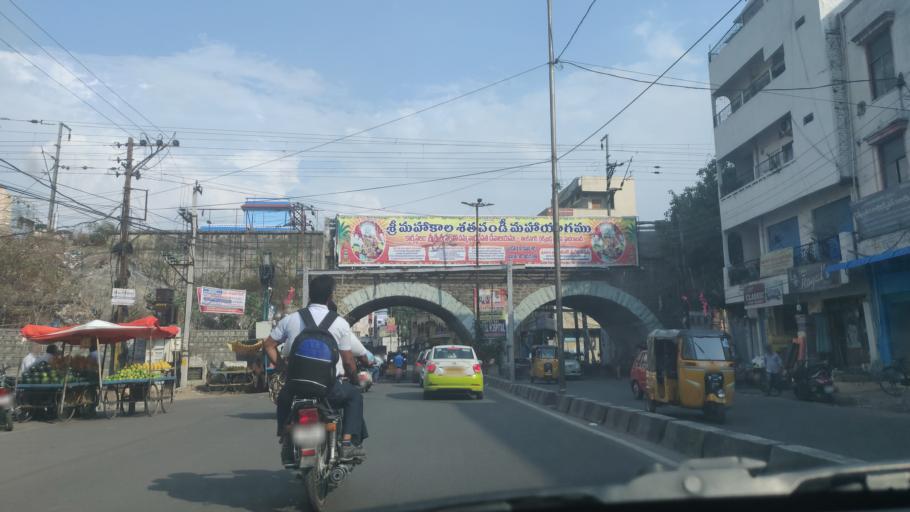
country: IN
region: Telangana
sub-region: Rangareddi
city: Gaddi Annaram
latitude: 17.3951
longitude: 78.5043
